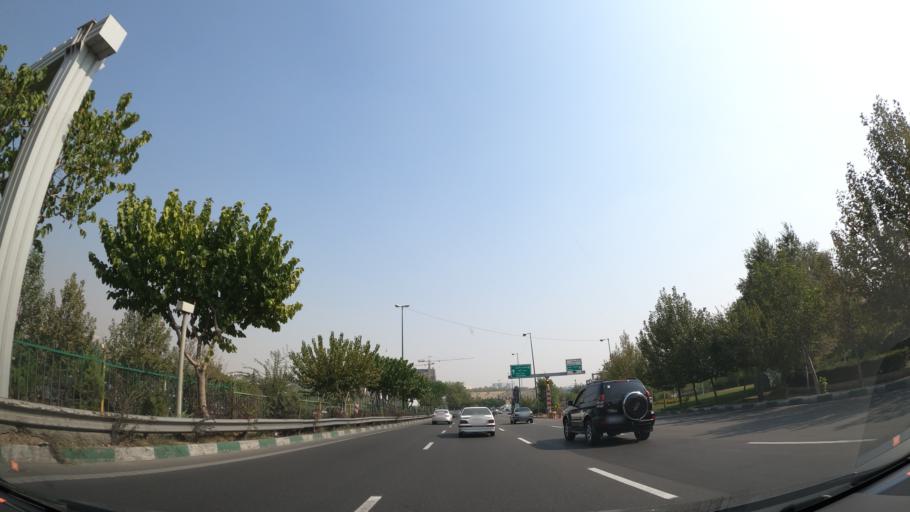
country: IR
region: Tehran
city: Shahr-e Qods
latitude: 35.7573
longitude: 51.2647
